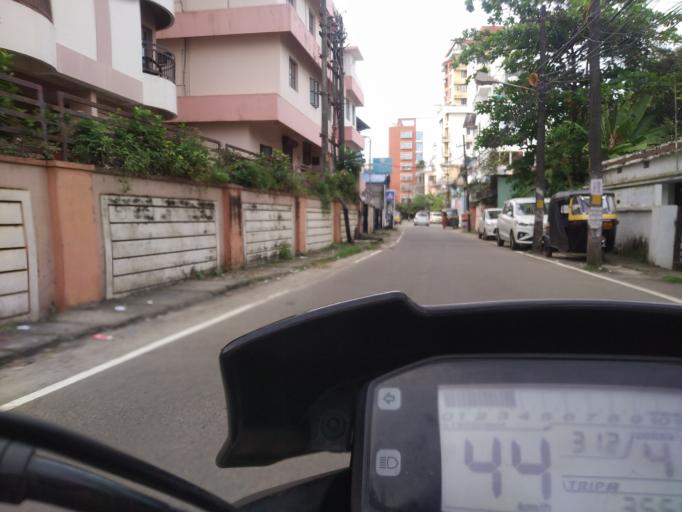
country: IN
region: Kerala
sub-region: Ernakulam
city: Cochin
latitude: 9.9701
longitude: 76.2888
